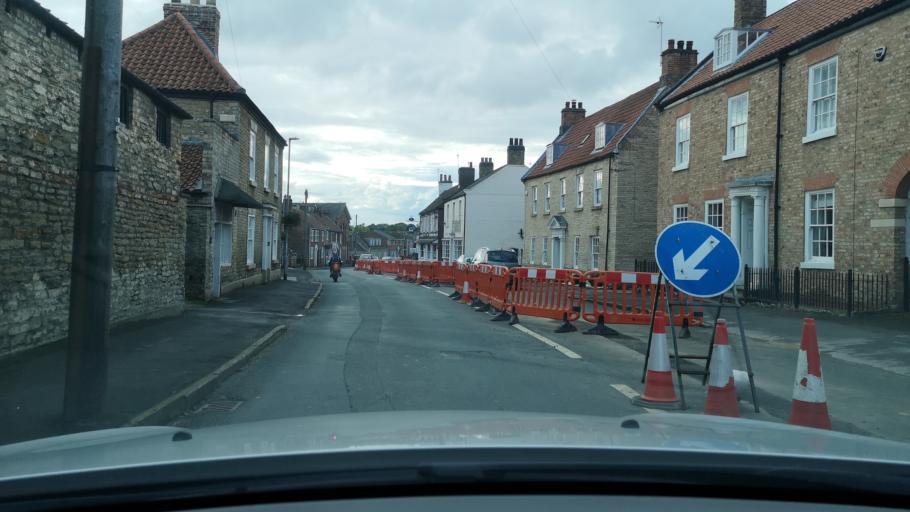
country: GB
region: England
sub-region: East Riding of Yorkshire
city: North Cave
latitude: 53.7804
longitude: -0.6455
